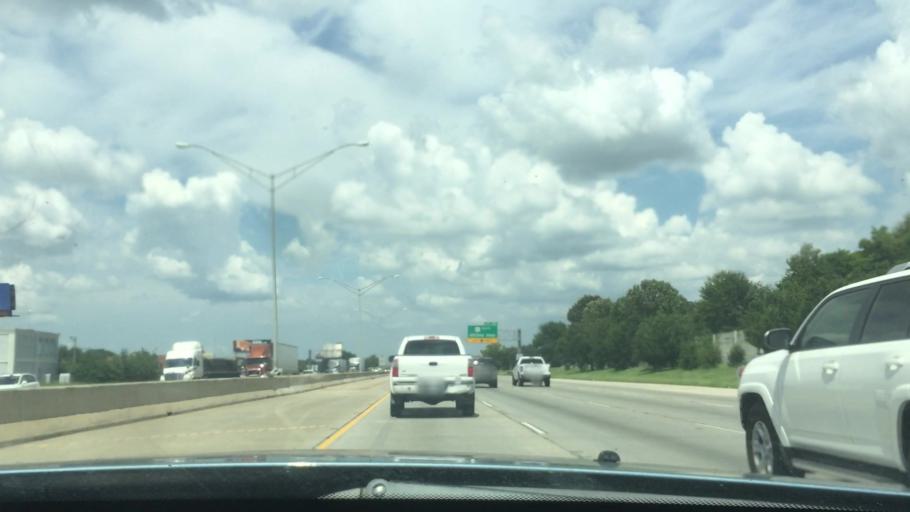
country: US
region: Louisiana
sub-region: East Baton Rouge Parish
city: Westminster
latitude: 30.4198
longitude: -91.0842
